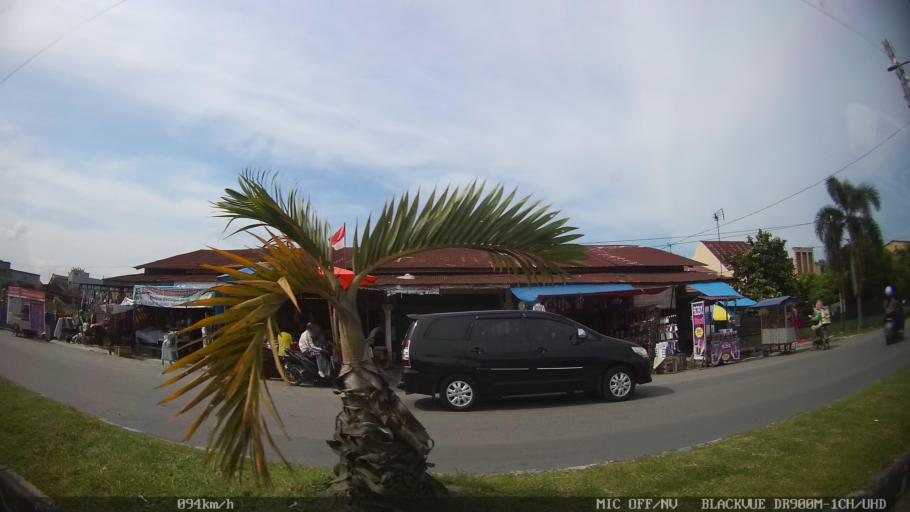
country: ID
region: North Sumatra
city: Percut
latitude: 3.6123
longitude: 98.8042
